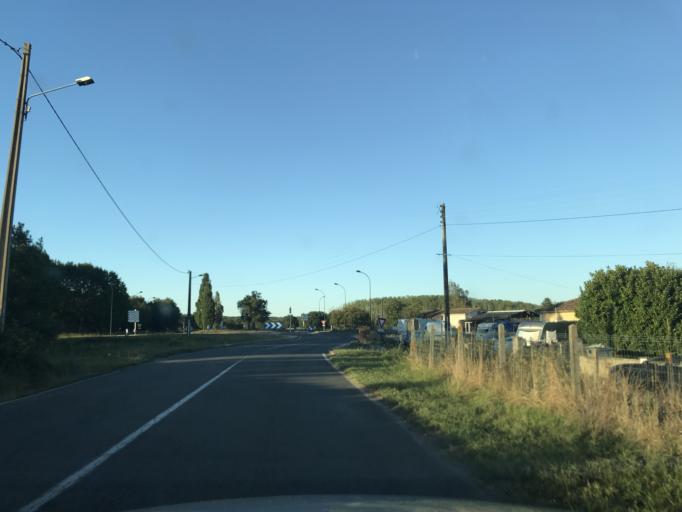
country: FR
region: Aquitaine
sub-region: Departement de la Gironde
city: Saint-Medard-de-Guizieres
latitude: 45.0285
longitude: -0.0563
